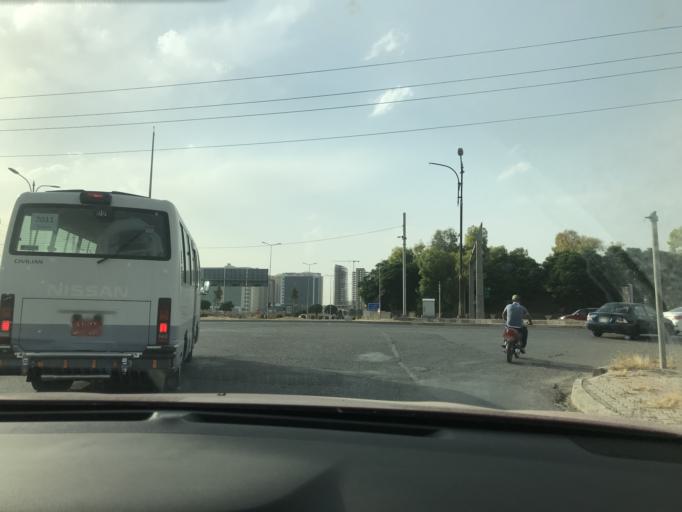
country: IQ
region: Arbil
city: Erbil
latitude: 36.1822
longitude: 43.9754
